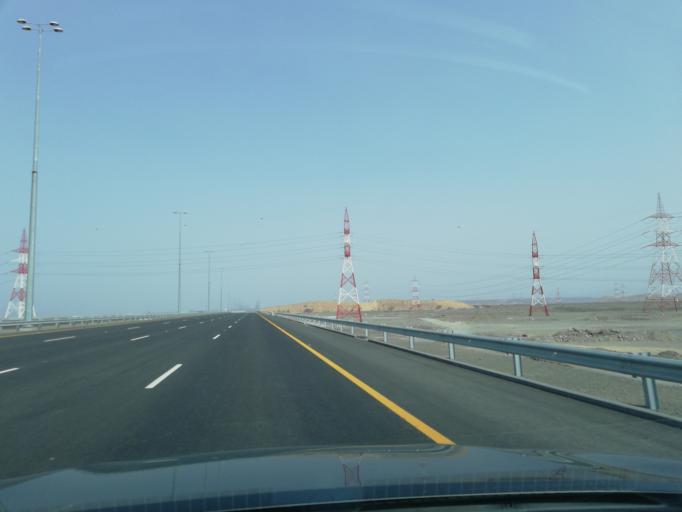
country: OM
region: Al Batinah
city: Al Sohar
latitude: 24.3272
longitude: 56.5639
